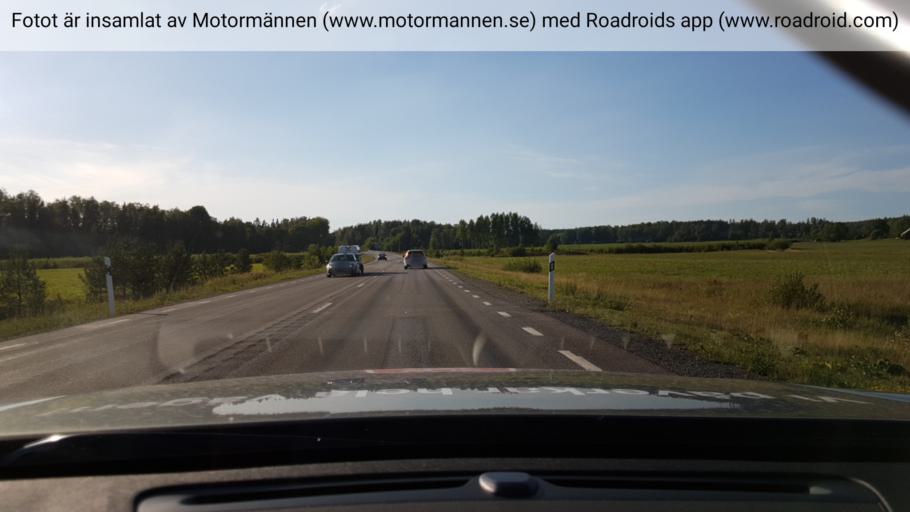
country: SE
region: Vaestmanland
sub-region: Kopings Kommun
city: Koping
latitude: 59.5473
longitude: 15.9231
